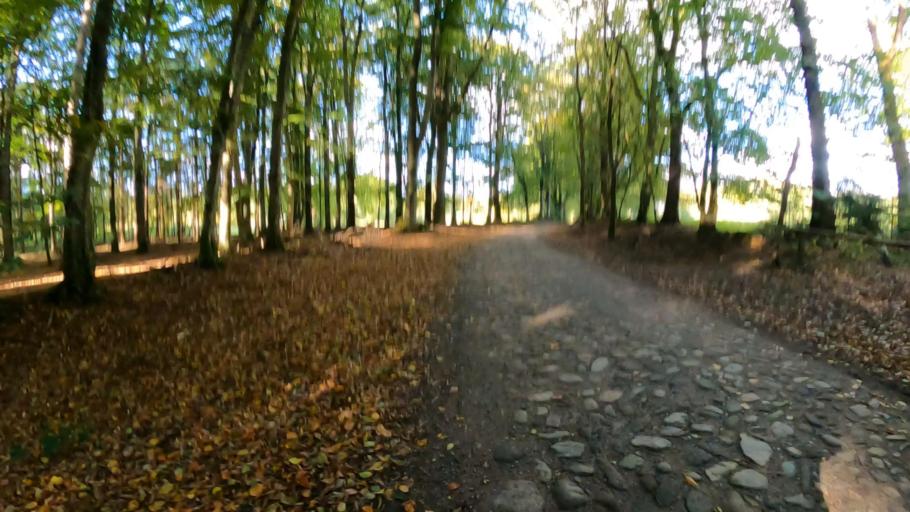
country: DE
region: Schleswig-Holstein
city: Heidmuhlen
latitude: 53.9517
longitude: 10.1234
